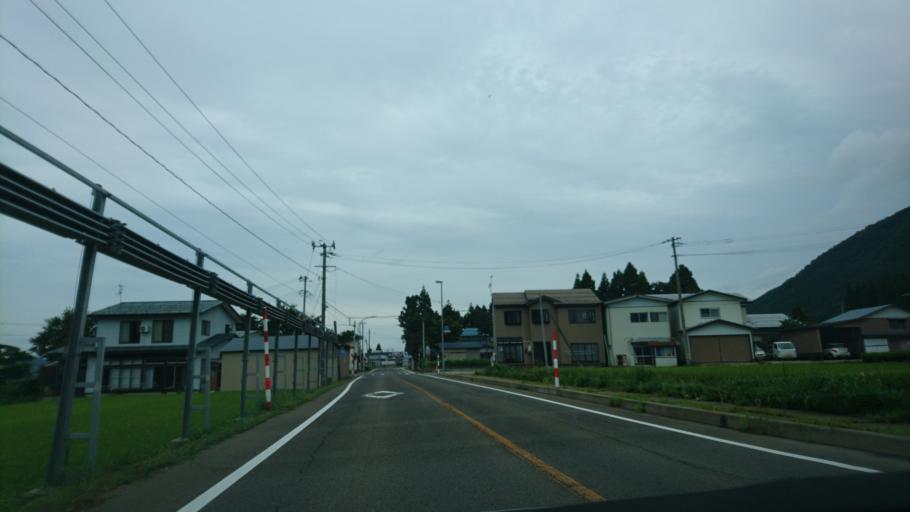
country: JP
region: Akita
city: Yuzawa
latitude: 39.1254
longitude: 140.5768
